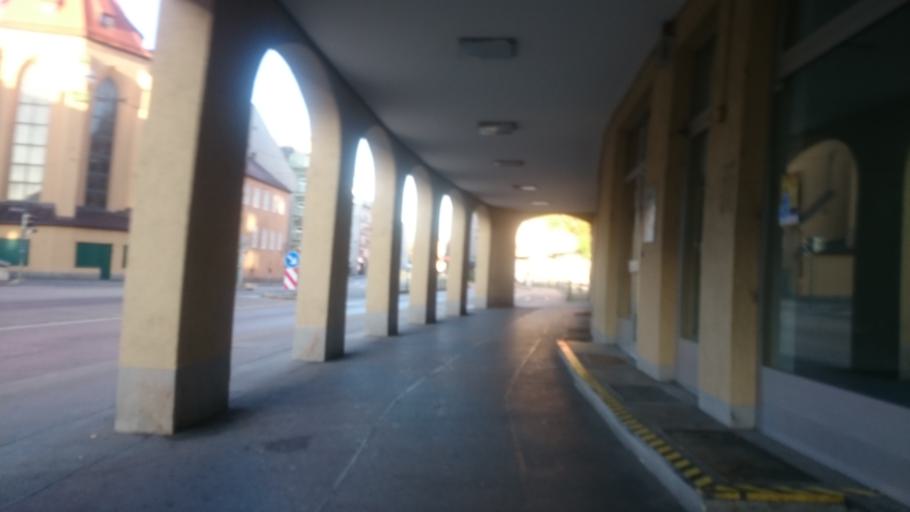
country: DE
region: Bavaria
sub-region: Swabia
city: Augsburg
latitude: 48.3703
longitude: 10.9059
